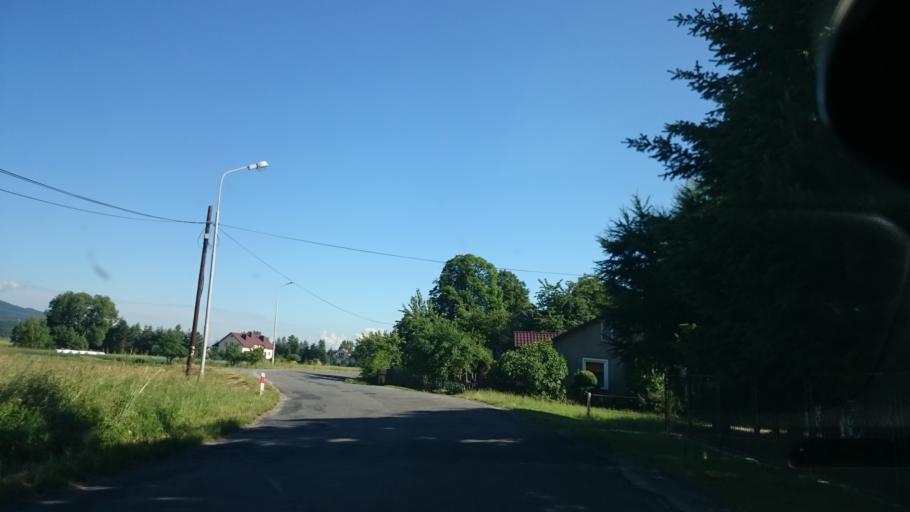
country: PL
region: Lower Silesian Voivodeship
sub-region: Powiat klodzki
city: Bystrzyca Klodzka
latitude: 50.2643
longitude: 16.6418
